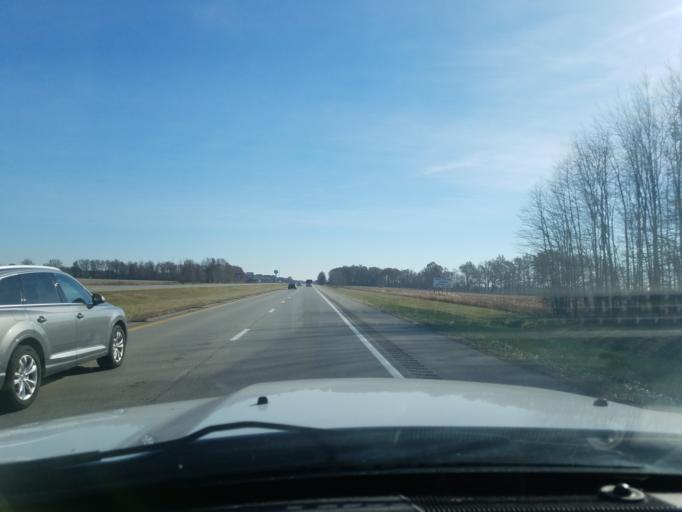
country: US
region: Ohio
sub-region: Brown County
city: Mount Orab
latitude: 39.0496
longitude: -83.9543
